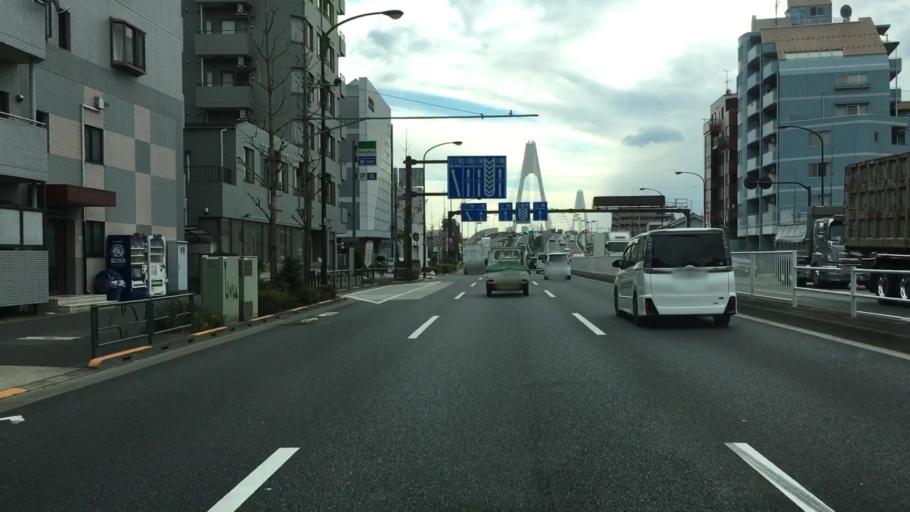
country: JP
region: Kanagawa
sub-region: Kawasaki-shi
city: Kawasaki
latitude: 35.5488
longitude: 139.7411
